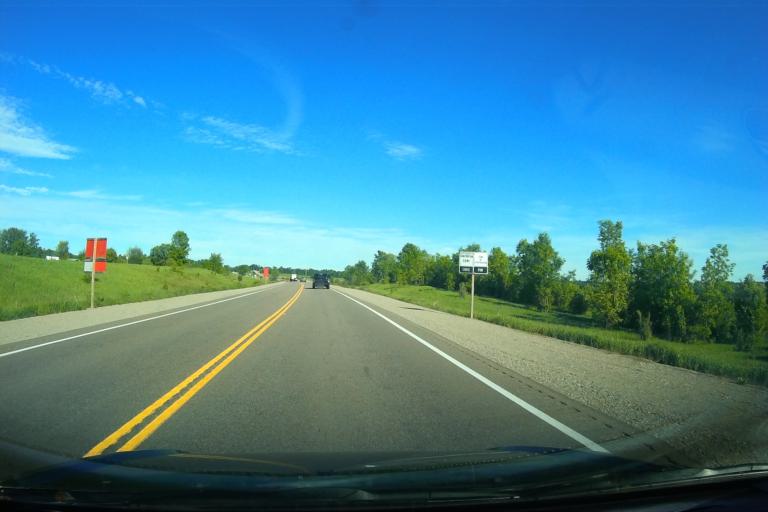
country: CA
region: Ontario
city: Pembroke
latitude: 45.7656
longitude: -77.0757
